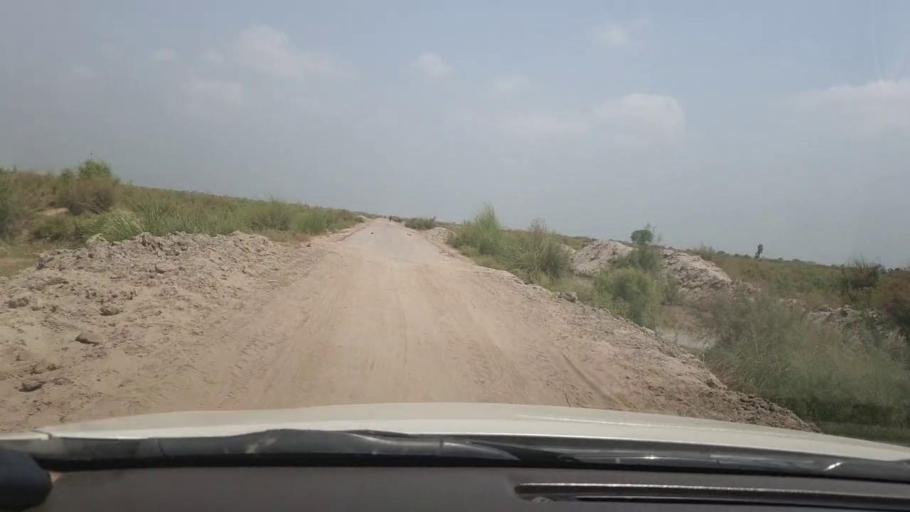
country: PK
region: Sindh
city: Garhi Yasin
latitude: 28.0177
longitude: 68.5000
